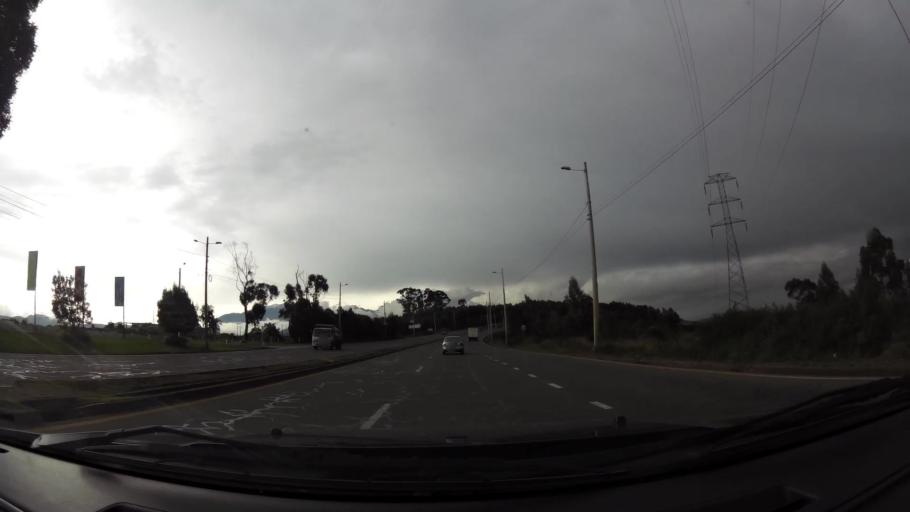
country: EC
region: Pichincha
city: Sangolqui
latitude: -0.3141
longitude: -78.5221
